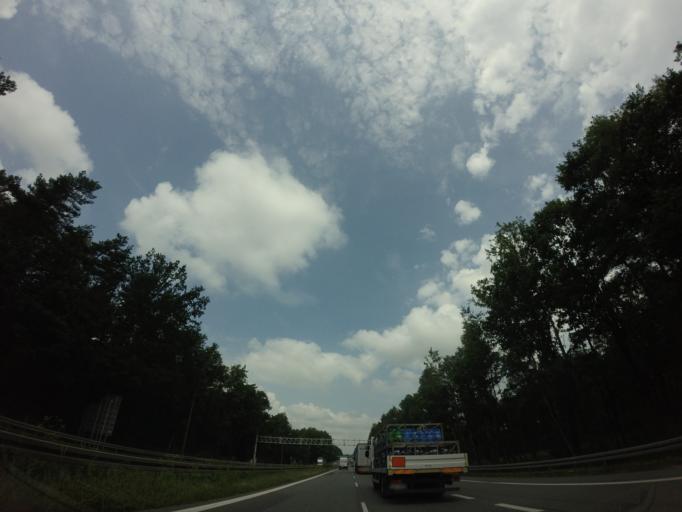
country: PL
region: Silesian Voivodeship
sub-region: Myslowice
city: Myslowice
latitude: 50.1785
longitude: 19.1684
